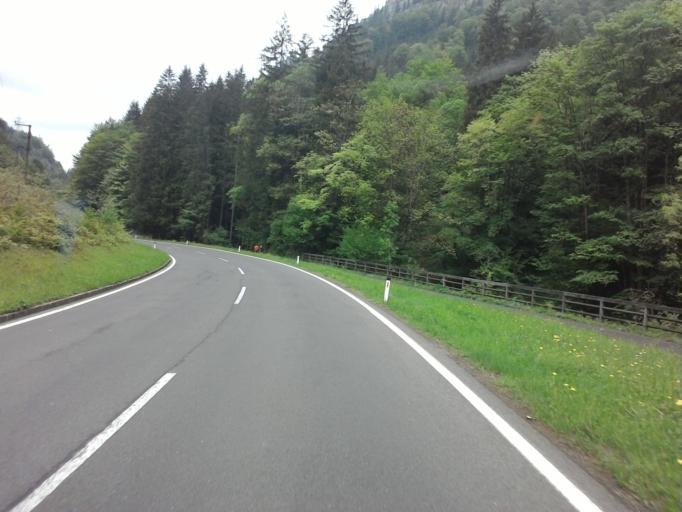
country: AT
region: Styria
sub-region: Politischer Bezirk Leoben
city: Eisenerz
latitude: 47.5833
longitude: 14.8223
